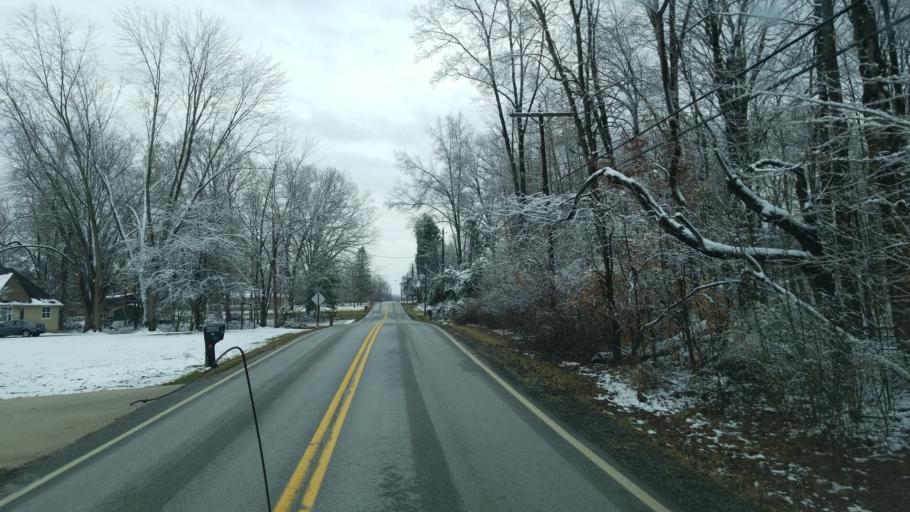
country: US
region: Ohio
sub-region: Portage County
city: Ravenna
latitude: 41.1706
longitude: -81.2132
